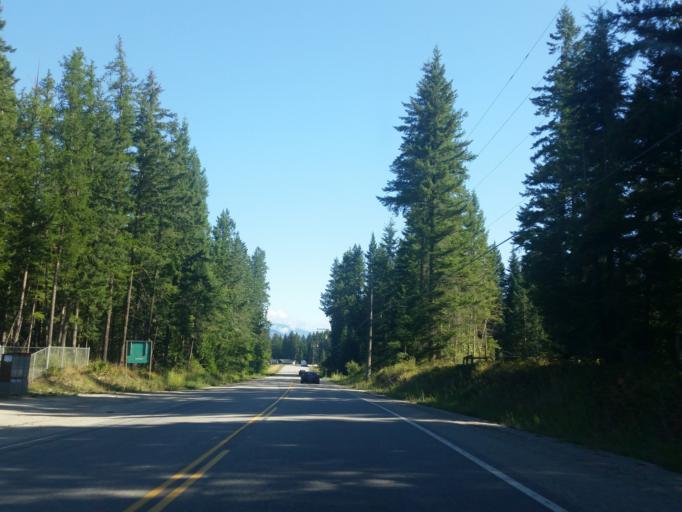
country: CA
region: British Columbia
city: Enderby
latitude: 50.6775
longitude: -119.0551
